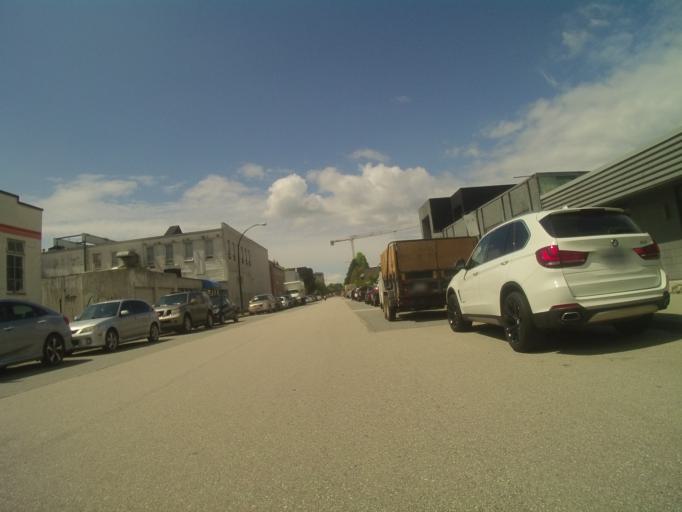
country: CA
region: British Columbia
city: Vancouver
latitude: 49.2666
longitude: -123.1068
